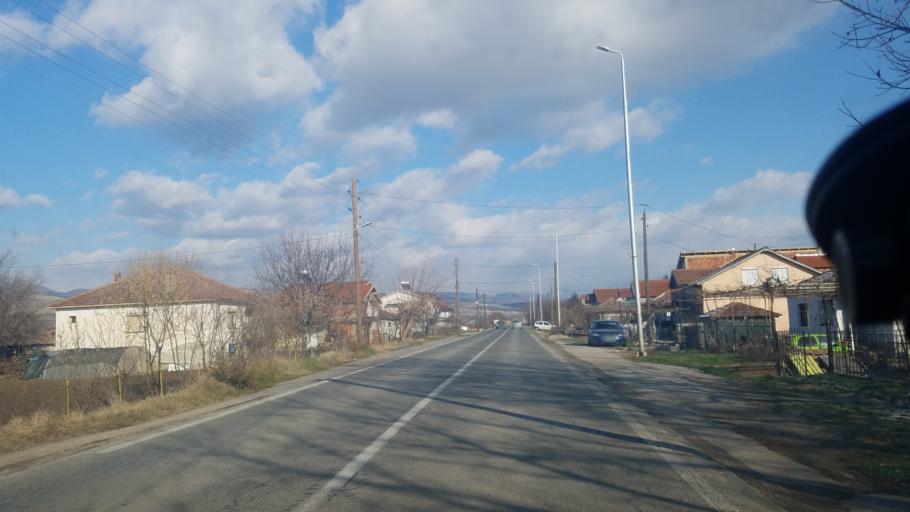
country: MK
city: Obleshevo
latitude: 41.8860
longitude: 22.3389
